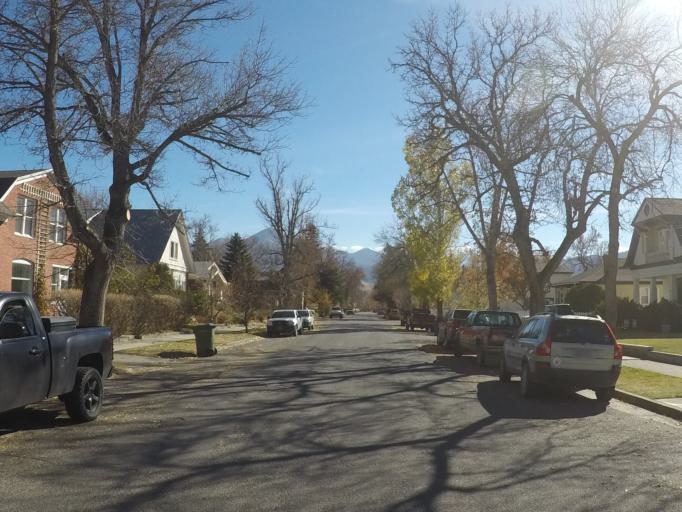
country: US
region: Montana
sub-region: Park County
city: Livingston
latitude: 45.6575
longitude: -110.5630
